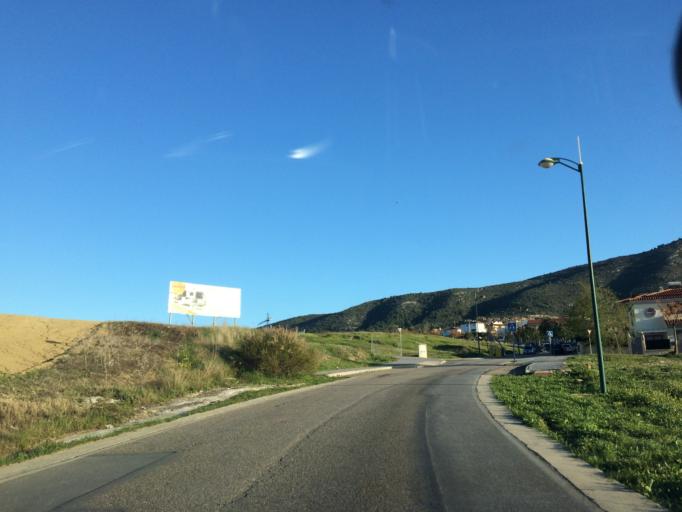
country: ES
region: Andalusia
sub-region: Provincia de Malaga
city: Alhaurin de la Torre
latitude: 36.6681
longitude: -4.5361
